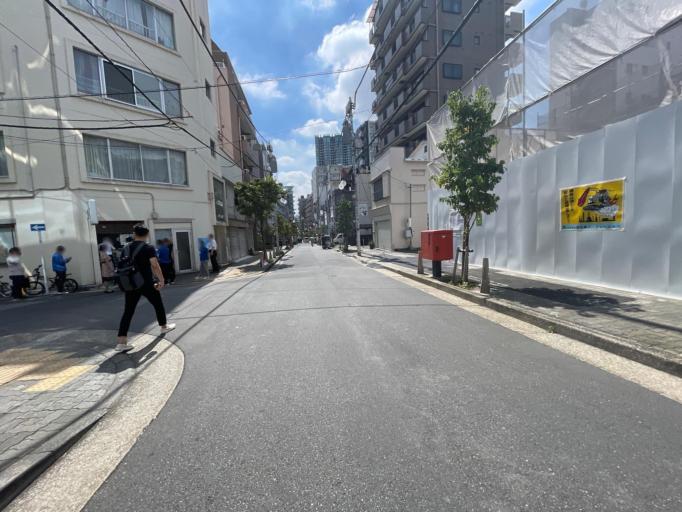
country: JP
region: Tokyo
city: Tokyo
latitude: 35.6571
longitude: 139.7428
